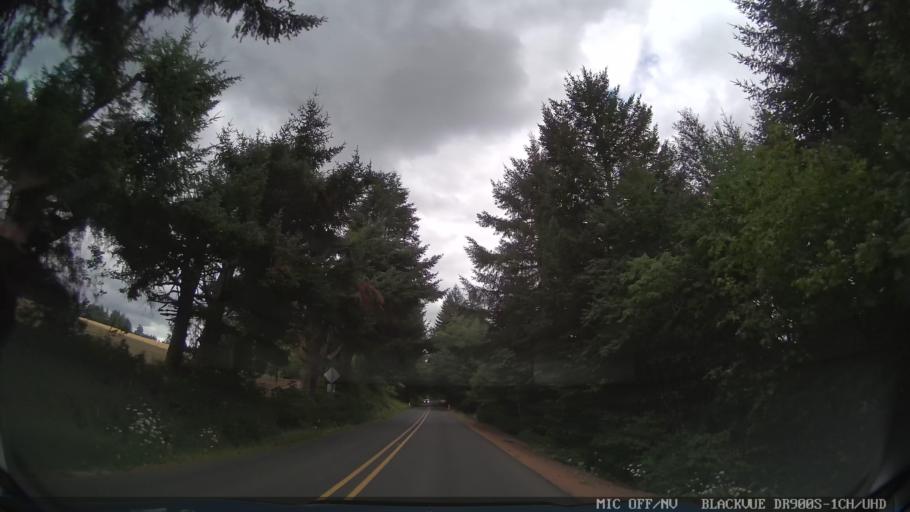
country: US
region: Oregon
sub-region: Linn County
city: Lyons
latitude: 44.8489
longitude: -122.6735
